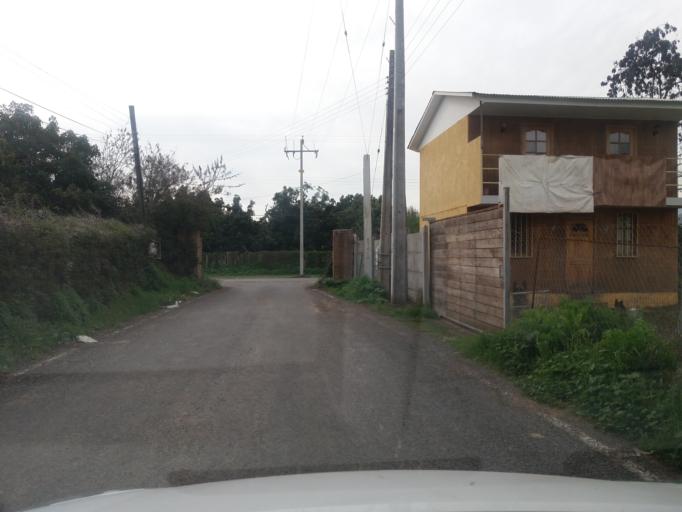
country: CL
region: Valparaiso
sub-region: Provincia de Quillota
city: Hacienda La Calera
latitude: -32.7580
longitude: -71.1732
